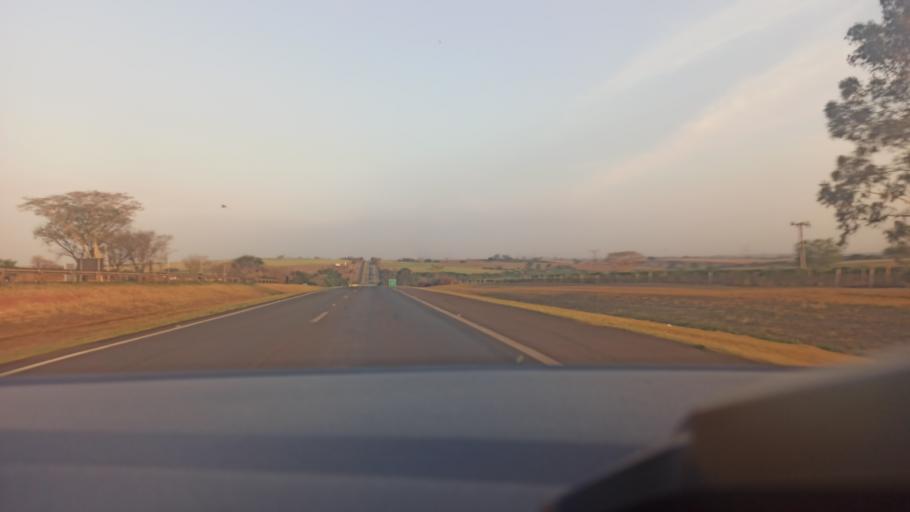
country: BR
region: Sao Paulo
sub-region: Santa Adelia
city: Santa Adelia
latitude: -21.3658
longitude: -48.7571
